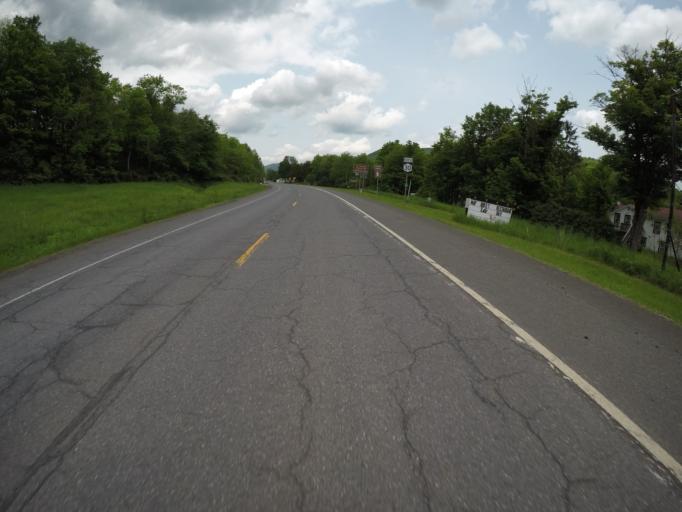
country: US
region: New York
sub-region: Delaware County
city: Stamford
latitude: 42.3018
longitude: -74.5548
